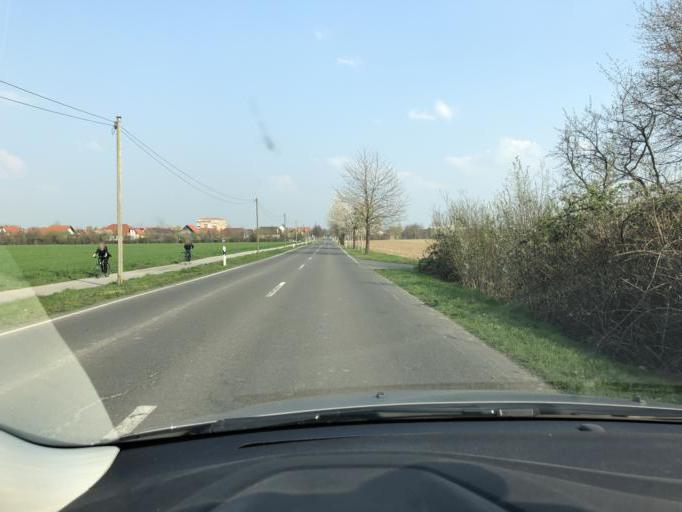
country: DE
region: Saxony
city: Rackwitz
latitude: 51.4330
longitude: 12.3592
